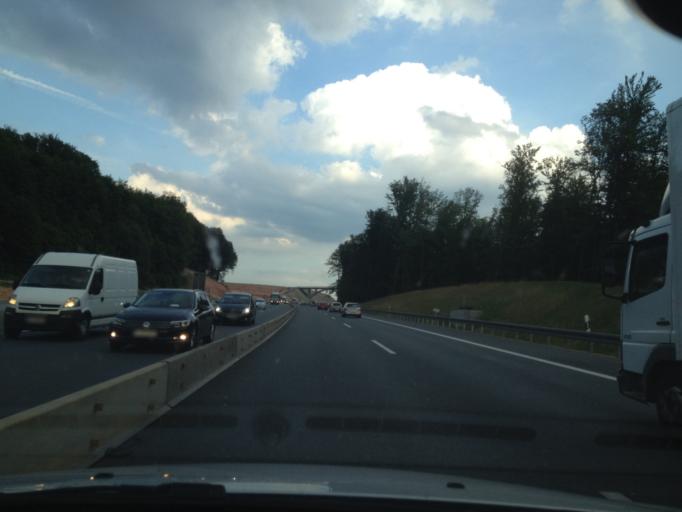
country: DE
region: Bavaria
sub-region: Regierungsbezirk Unterfranken
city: Weibersbrunn
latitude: 49.9436
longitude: 9.3384
